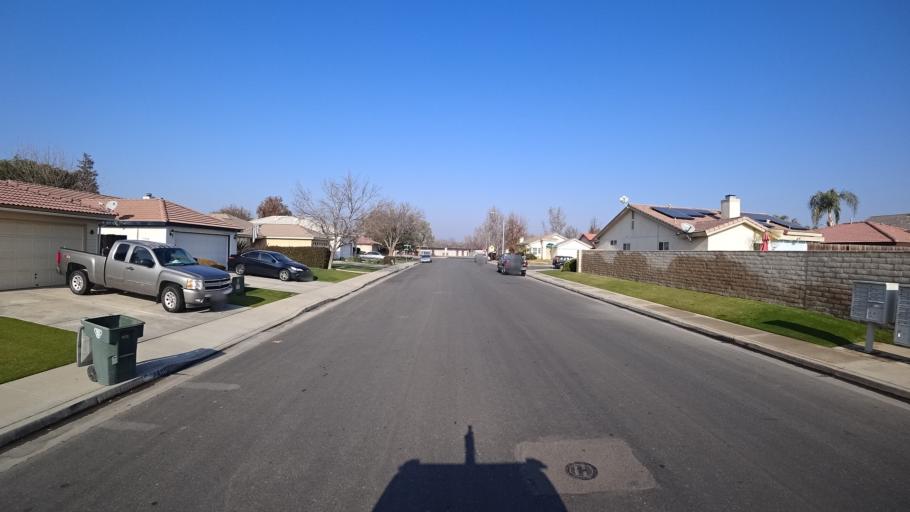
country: US
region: California
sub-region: Kern County
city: Greenacres
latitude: 35.3904
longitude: -119.1043
